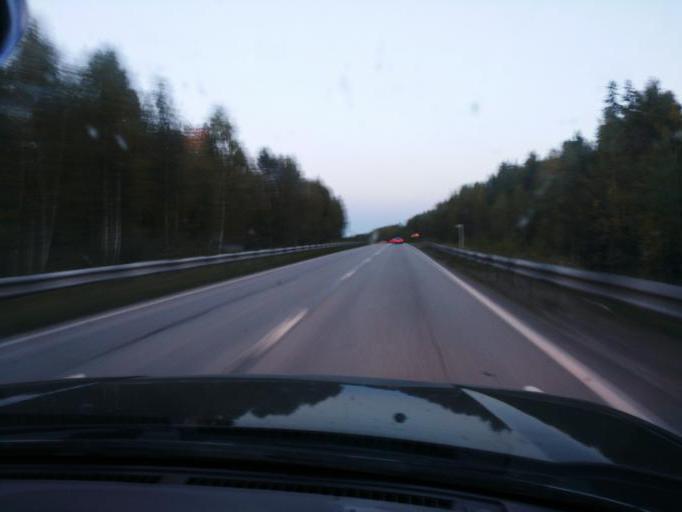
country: RU
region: Perm
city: Verkhnechusovskiye Gorodki
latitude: 58.2492
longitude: 57.0163
